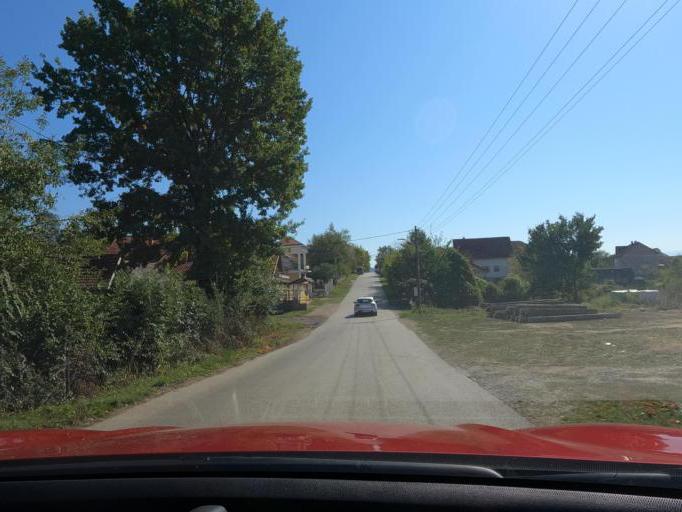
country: RS
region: Central Serbia
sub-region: Raski Okrug
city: Kraljevo
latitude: 43.7525
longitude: 20.7007
